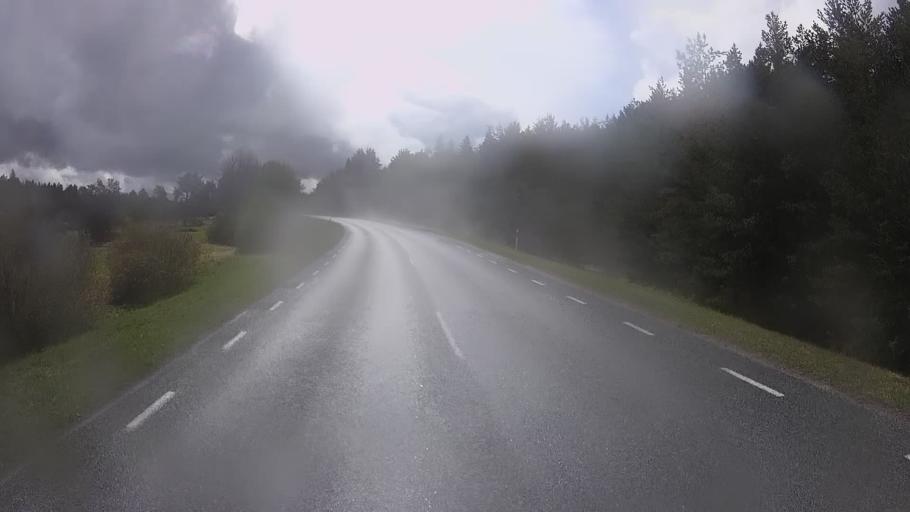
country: EE
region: Hiiumaa
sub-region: Kaerdla linn
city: Kardla
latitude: 58.9473
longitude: 22.7715
